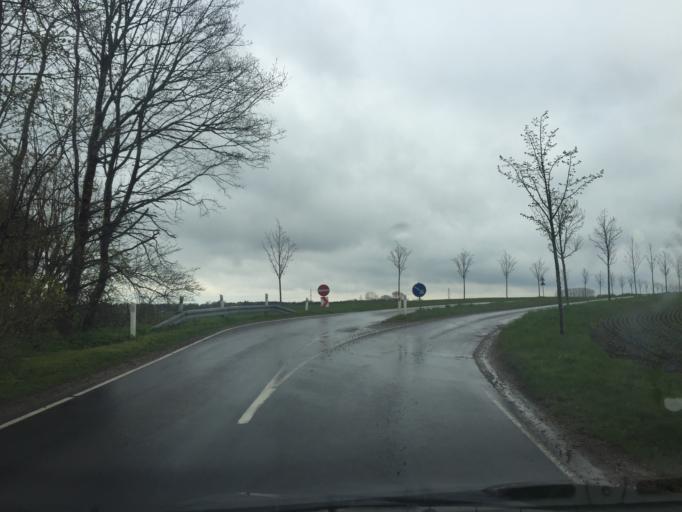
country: DK
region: Capital Region
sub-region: Hoje-Taastrup Kommune
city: Taastrup
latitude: 55.6944
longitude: 12.2492
